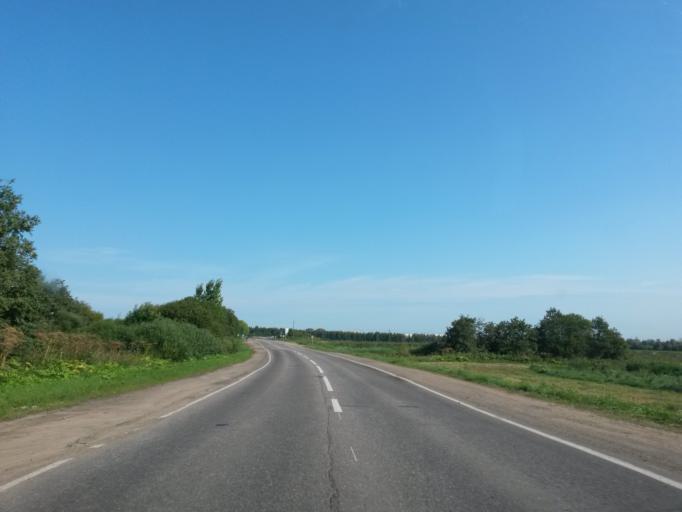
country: RU
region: Jaroslavl
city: Yaroslavl
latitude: 57.5485
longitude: 39.8620
